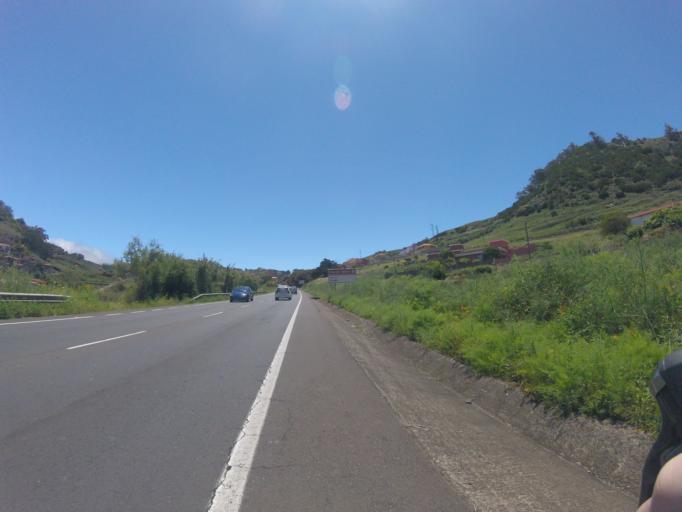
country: ES
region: Canary Islands
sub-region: Provincia de Santa Cruz de Tenerife
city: Tegueste
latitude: 28.5137
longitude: -16.3121
